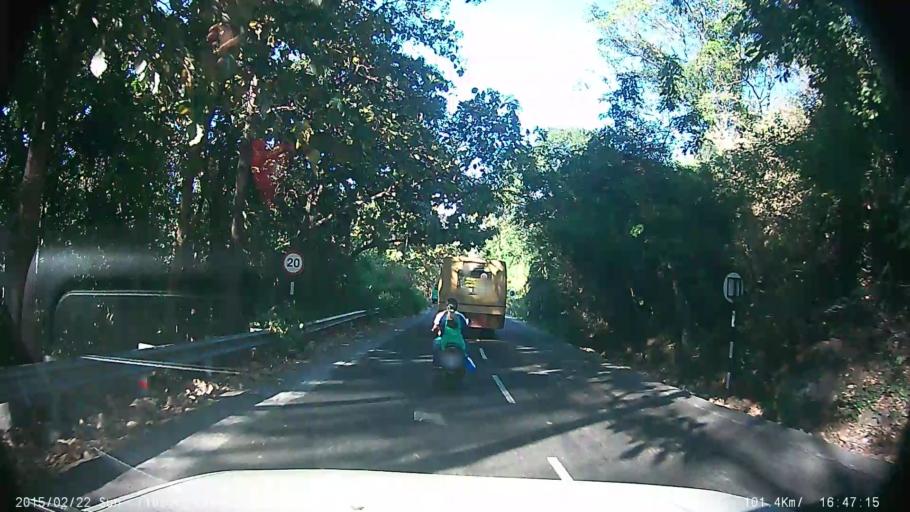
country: IN
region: Tamil Nadu
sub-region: Theni
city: Gudalur
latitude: 9.6217
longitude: 77.1930
